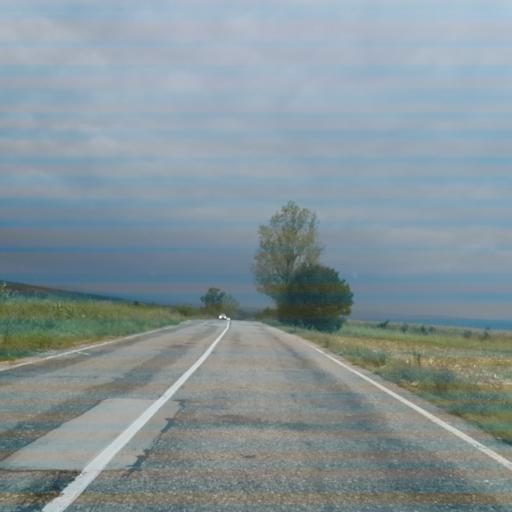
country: RS
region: Central Serbia
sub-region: Nisavski Okrug
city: Razanj
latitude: 43.6363
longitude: 21.5596
